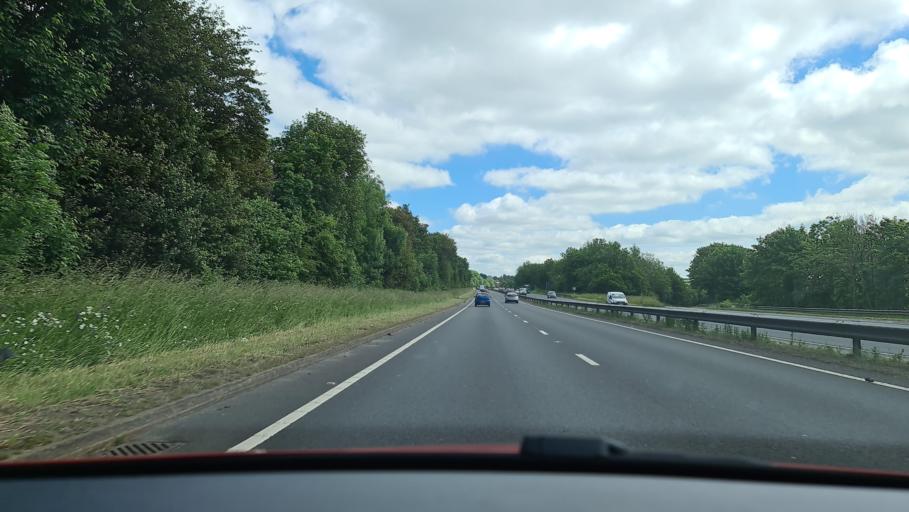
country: GB
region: England
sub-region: Devon
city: Yealmpton
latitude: 50.3840
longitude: -3.9735
